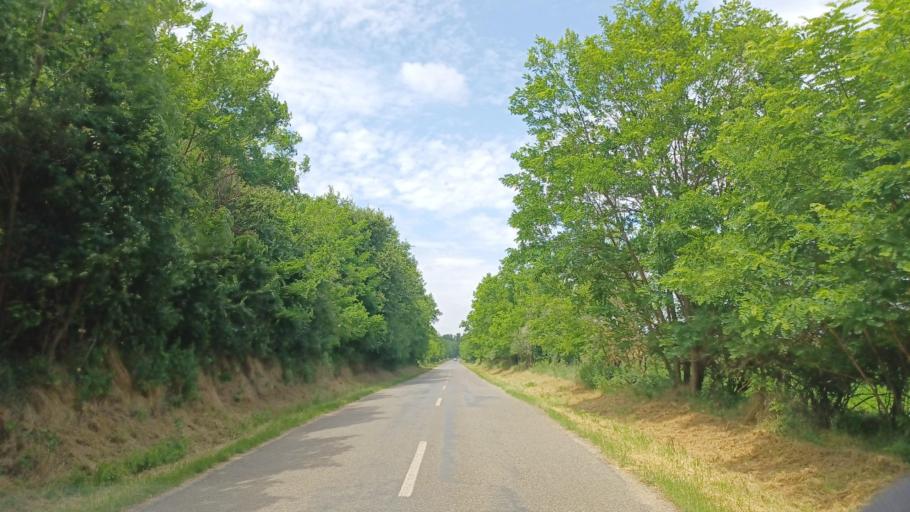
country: HU
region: Tolna
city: Simontornya
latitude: 46.7041
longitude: 18.5127
